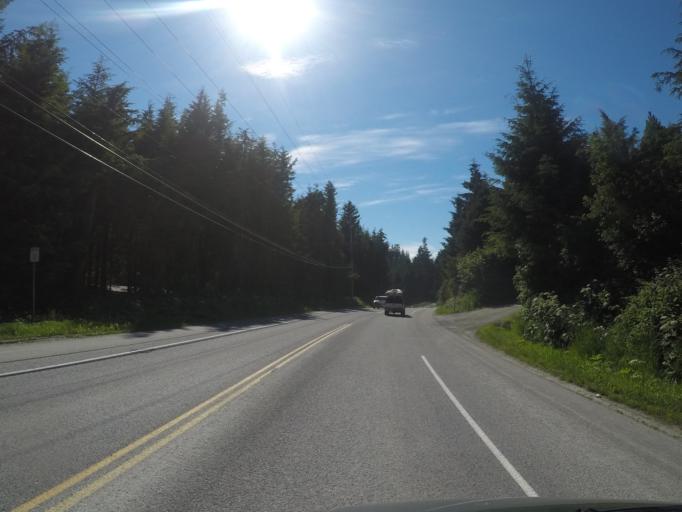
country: US
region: Alaska
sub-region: Juneau City and Borough
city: Juneau
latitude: 58.3832
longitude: -134.6640
